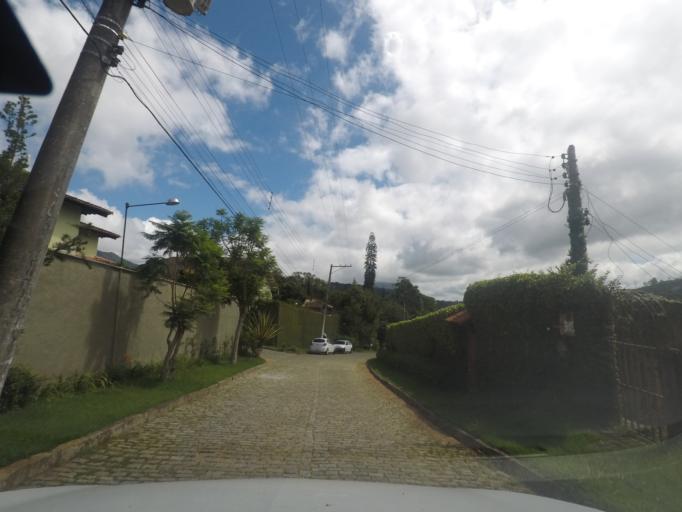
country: BR
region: Rio de Janeiro
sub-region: Teresopolis
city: Teresopolis
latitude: -22.3962
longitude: -42.9887
